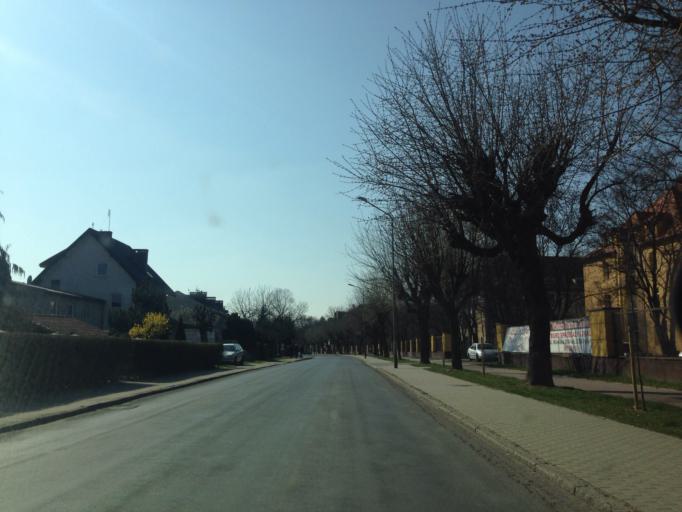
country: PL
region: Lower Silesian Voivodeship
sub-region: Powiat olesnicki
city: Olesnica
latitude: 51.2087
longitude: 17.4097
